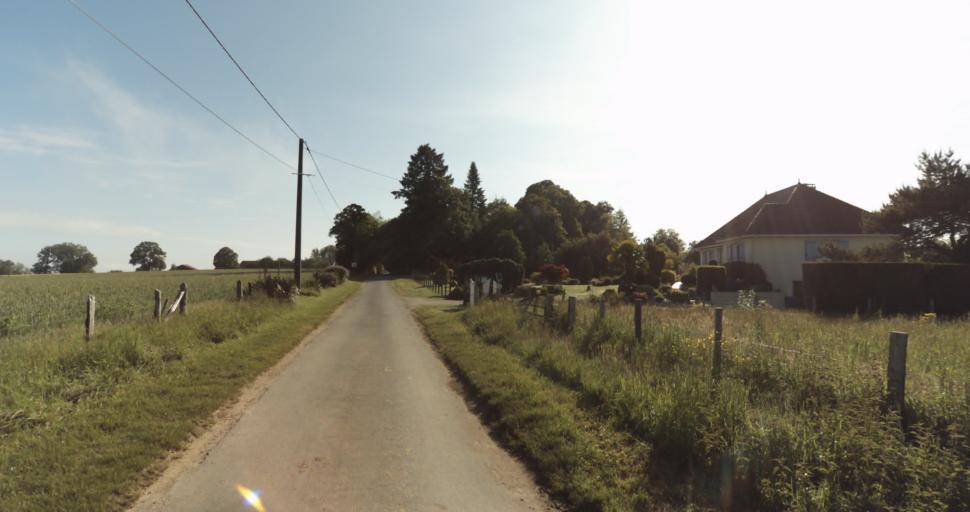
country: FR
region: Limousin
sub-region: Departement de la Haute-Vienne
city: Solignac
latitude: 45.7432
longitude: 1.2682
